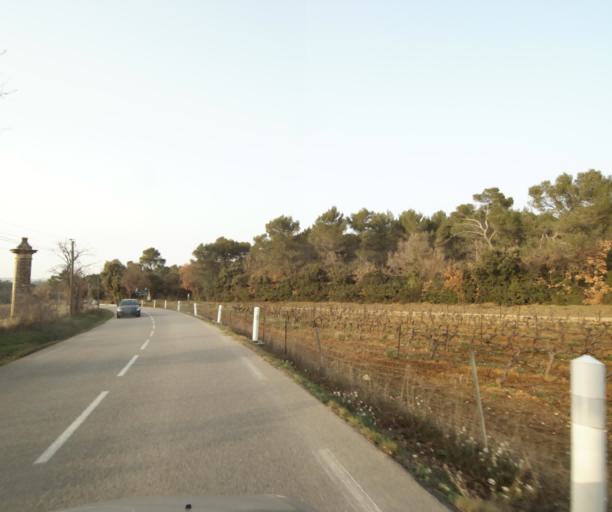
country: FR
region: Provence-Alpes-Cote d'Azur
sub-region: Departement des Bouches-du-Rhone
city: Rognes
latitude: 43.6374
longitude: 5.3610
